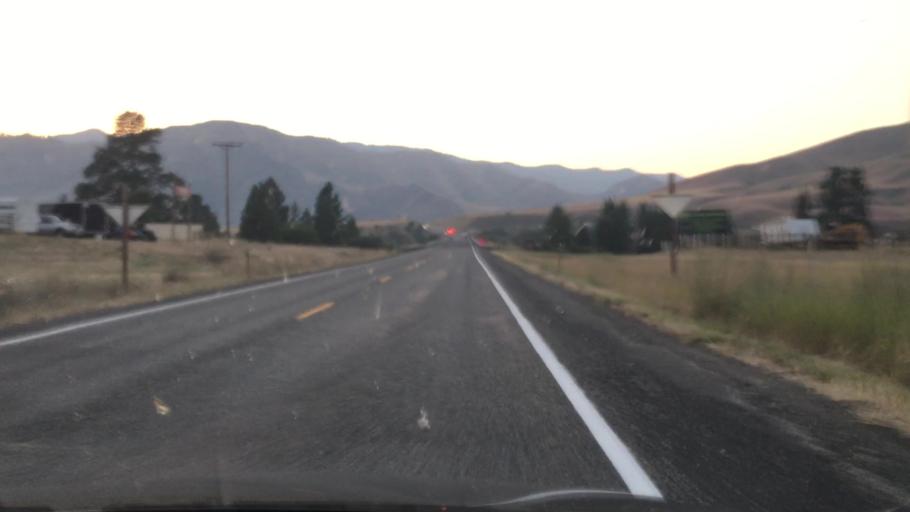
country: US
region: Idaho
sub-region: Idaho County
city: Grangeville
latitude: 45.6642
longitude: -116.2945
